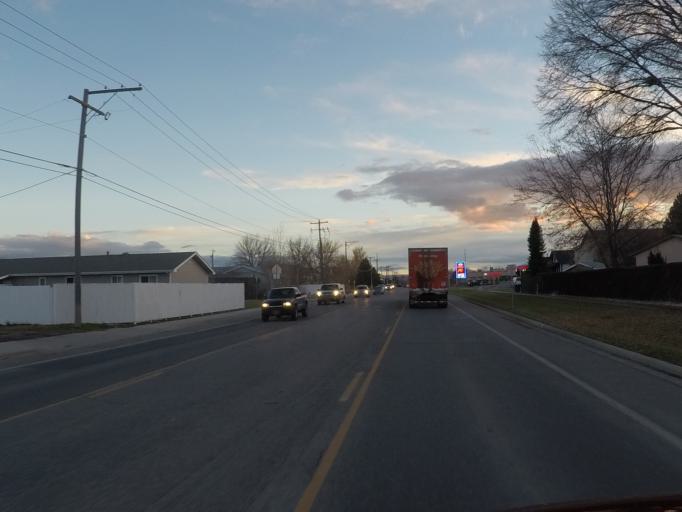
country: US
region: Montana
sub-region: Yellowstone County
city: Billings
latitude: 45.7585
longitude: -108.5969
